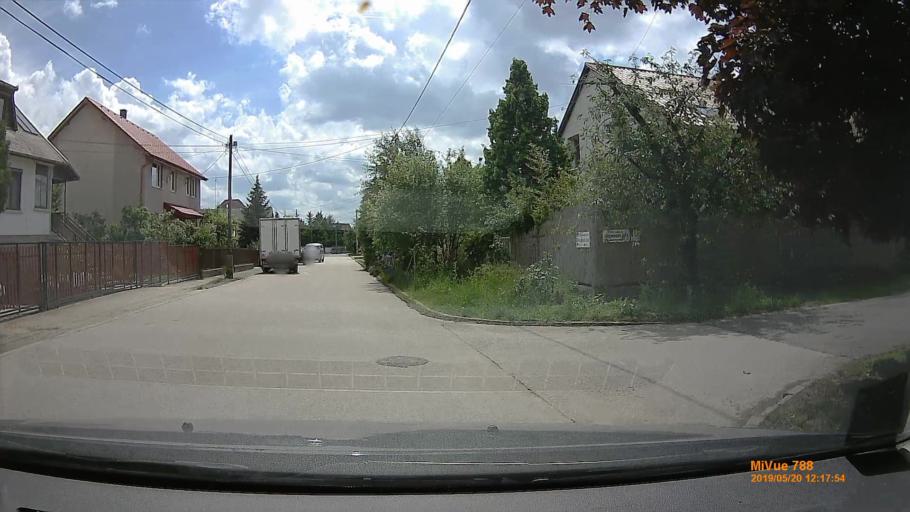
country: HU
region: Budapest
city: Budapest XVII. keruelet
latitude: 47.4992
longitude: 19.2787
